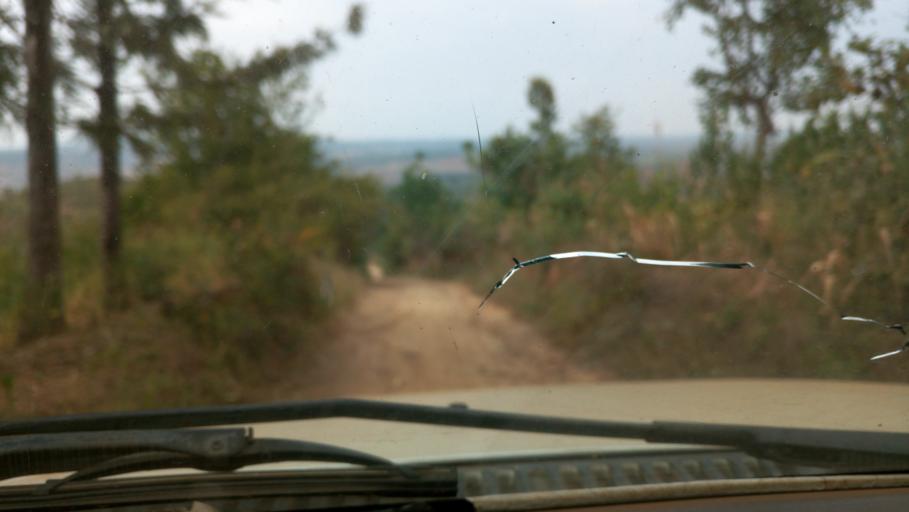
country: KE
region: Murang'a District
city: Maragua
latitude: -0.8215
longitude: 37.1912
